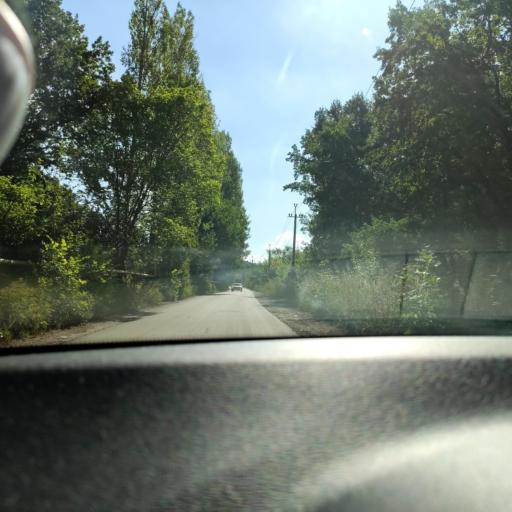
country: RU
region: Samara
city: Volzhskiy
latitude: 53.4326
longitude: 50.0819
